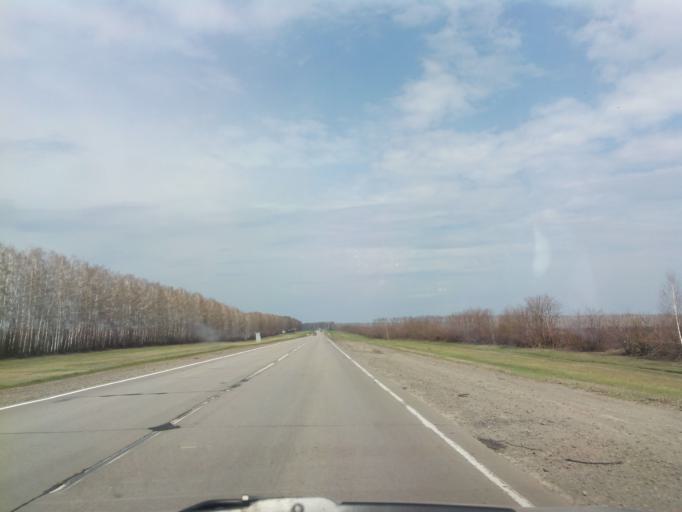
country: RU
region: Tambov
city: Zherdevka
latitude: 52.0744
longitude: 41.6619
